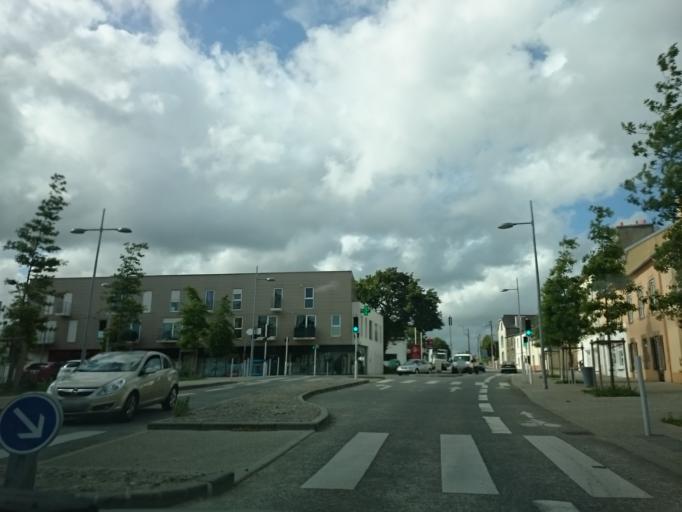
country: FR
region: Brittany
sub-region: Departement du Finistere
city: Brest
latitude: 48.4122
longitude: -4.4684
